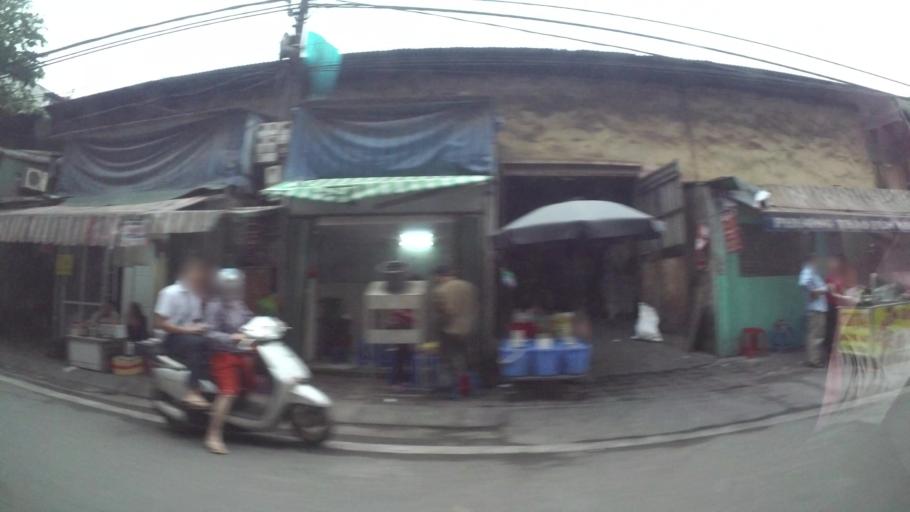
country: VN
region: Ha Noi
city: Hai BaTrung
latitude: 21.0106
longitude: 105.8675
